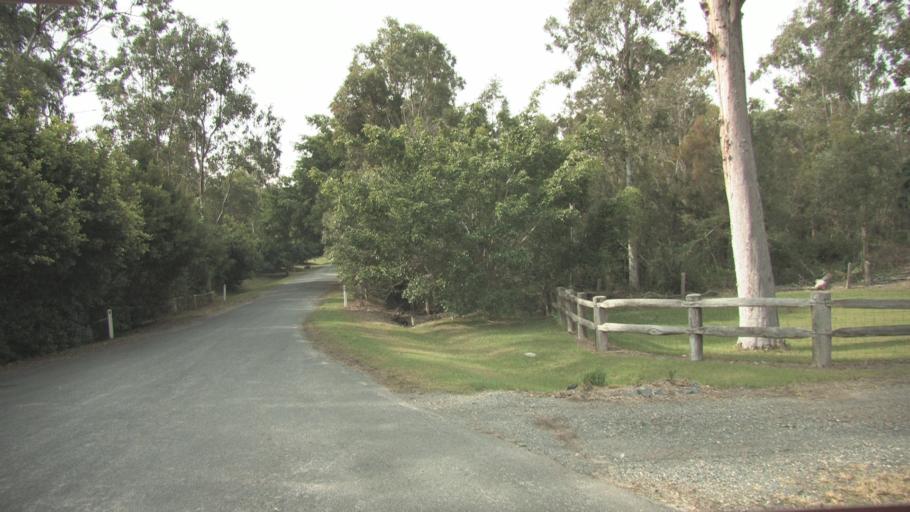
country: AU
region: Queensland
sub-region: Logan
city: Waterford West
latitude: -27.7335
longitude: 153.1353
